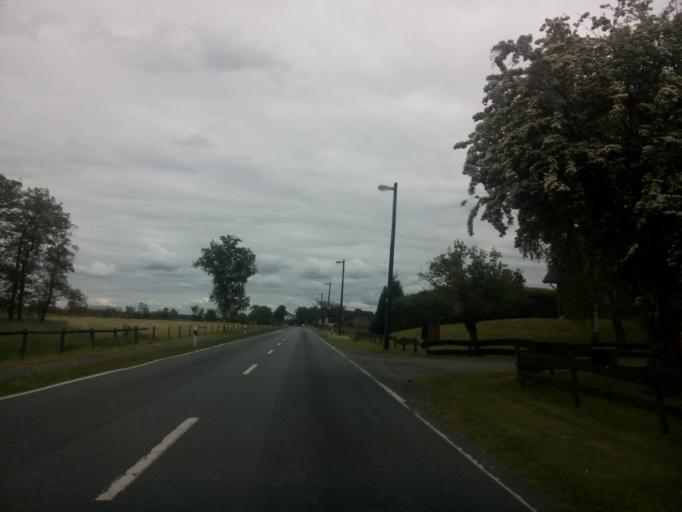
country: DE
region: Lower Saxony
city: Delmenhorst
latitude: 53.0872
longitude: 8.6786
